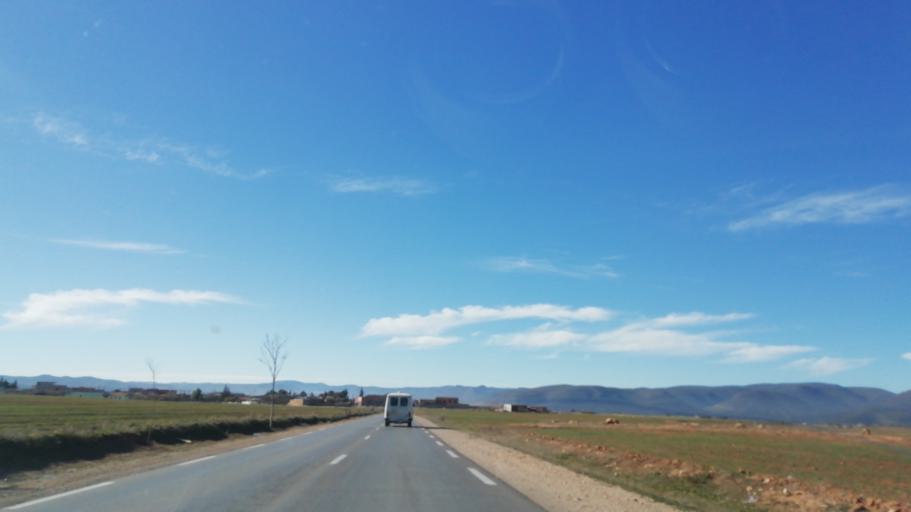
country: DZ
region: Tlemcen
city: Sebdou
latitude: 34.6675
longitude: -1.2833
